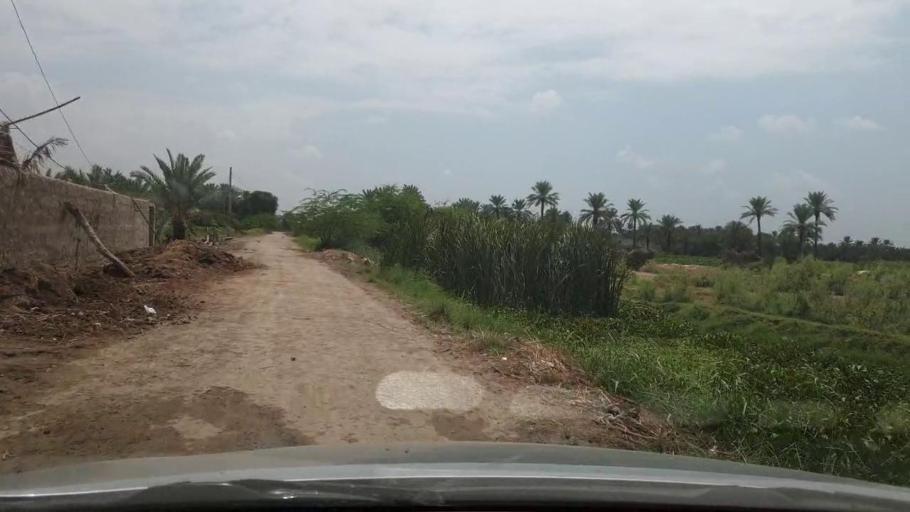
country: PK
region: Sindh
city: Kot Diji
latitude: 27.4202
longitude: 68.7593
